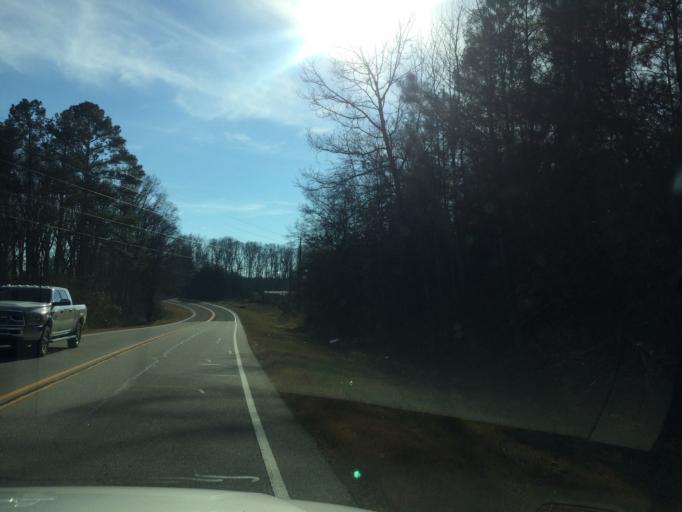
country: US
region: Georgia
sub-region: Franklin County
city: Lavonia
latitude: 34.4288
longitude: -83.0267
